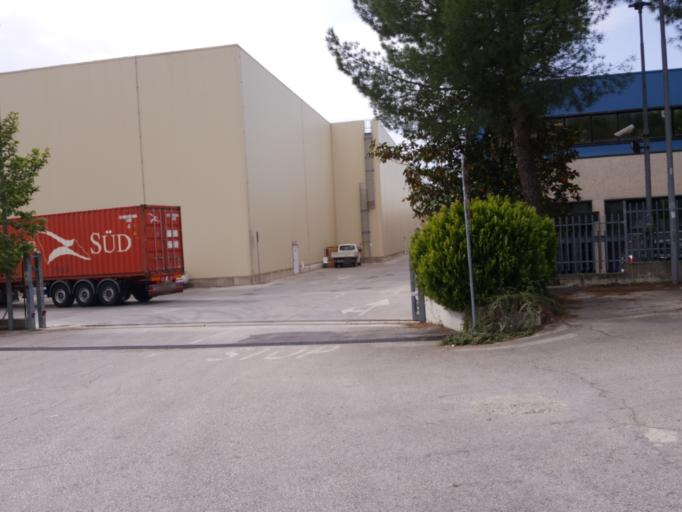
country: IT
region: The Marches
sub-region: Provincia di Ancona
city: Pianello Vallesina
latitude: 43.5051
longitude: 13.1702
